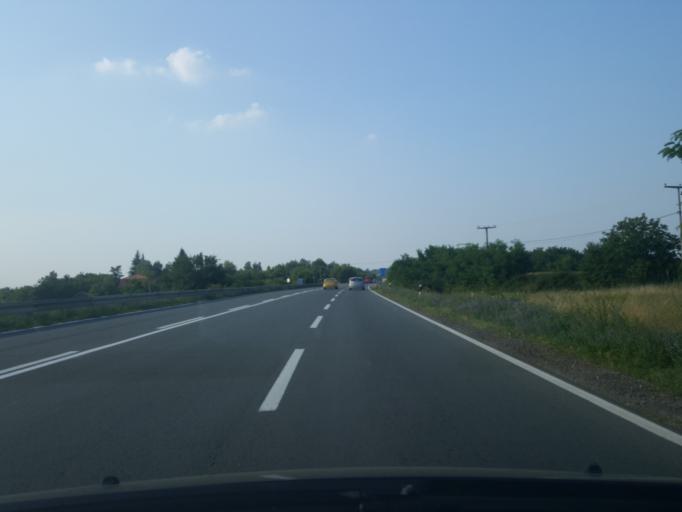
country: RS
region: Central Serbia
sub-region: Belgrade
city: Sopot
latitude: 44.5177
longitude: 20.6529
